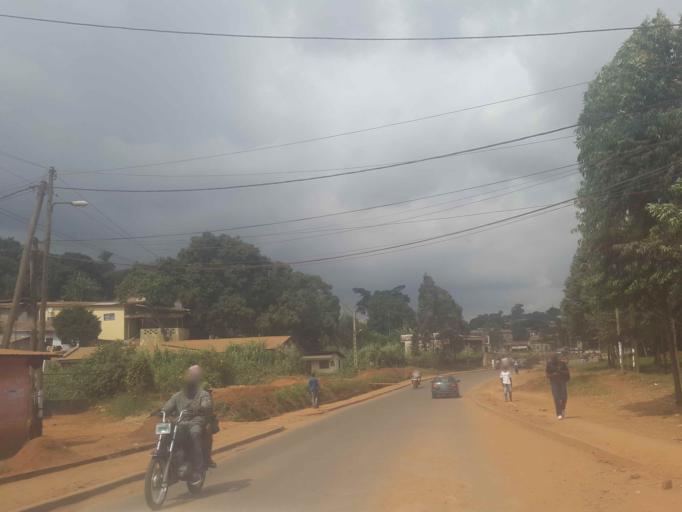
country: CM
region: Centre
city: Yaounde
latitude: 3.8716
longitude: 11.4824
